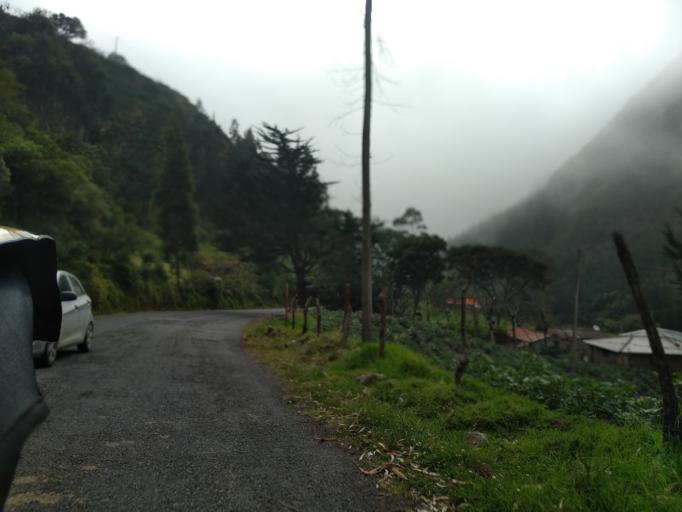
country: EC
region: Cotopaxi
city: Saquisili
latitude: -0.7001
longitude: -78.8046
